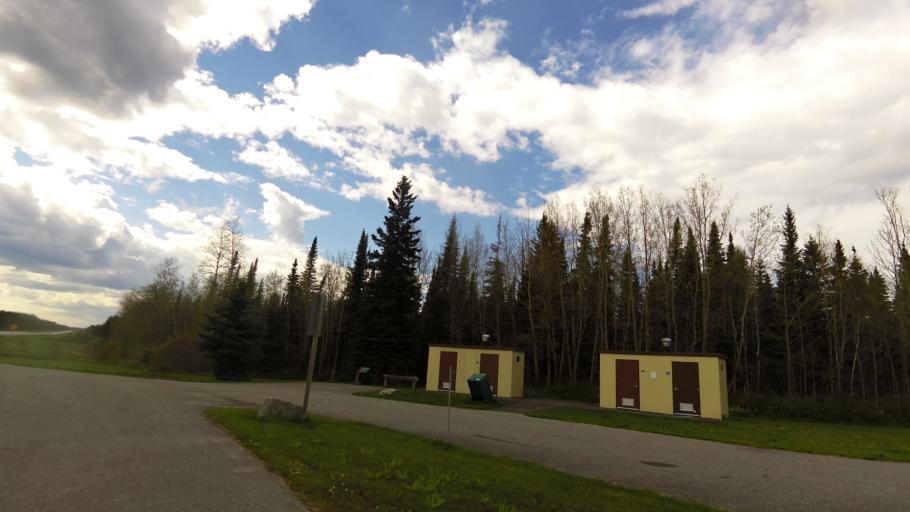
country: CA
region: Ontario
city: Hearst
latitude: 49.7314
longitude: -83.9136
